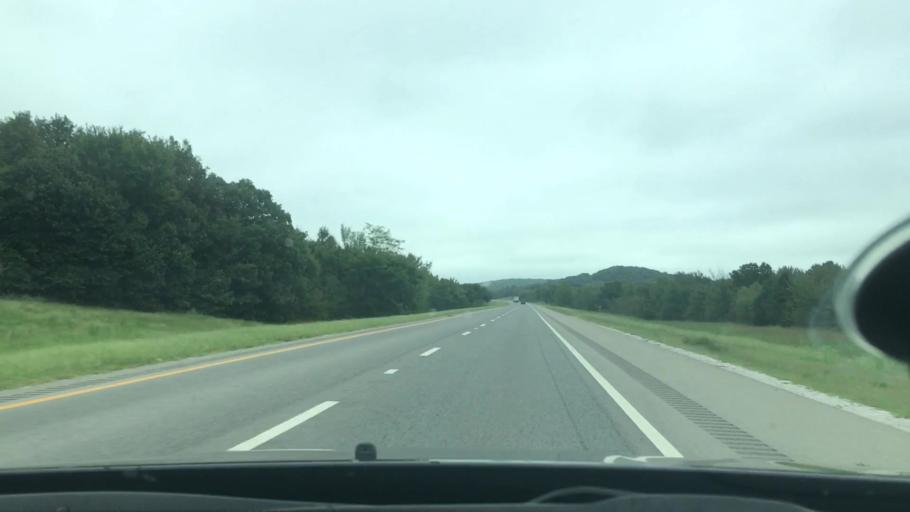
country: US
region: Oklahoma
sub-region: Muskogee County
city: Warner
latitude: 35.4566
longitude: -95.4109
